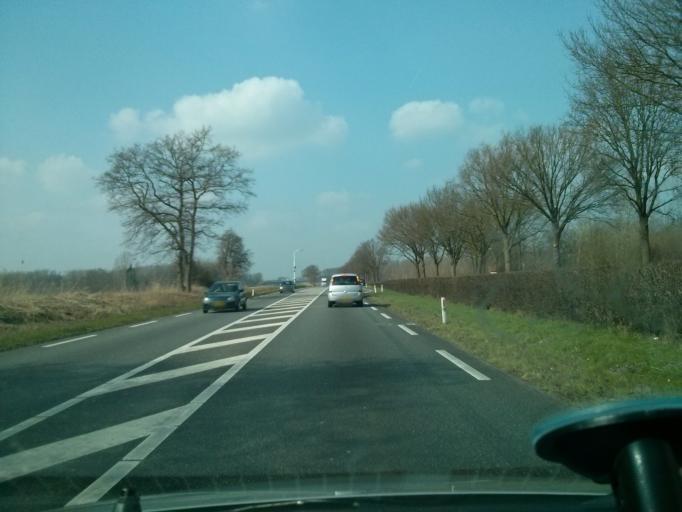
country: NL
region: North Brabant
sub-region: Gemeente Veghel
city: Eerde
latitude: 51.6365
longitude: 5.4803
